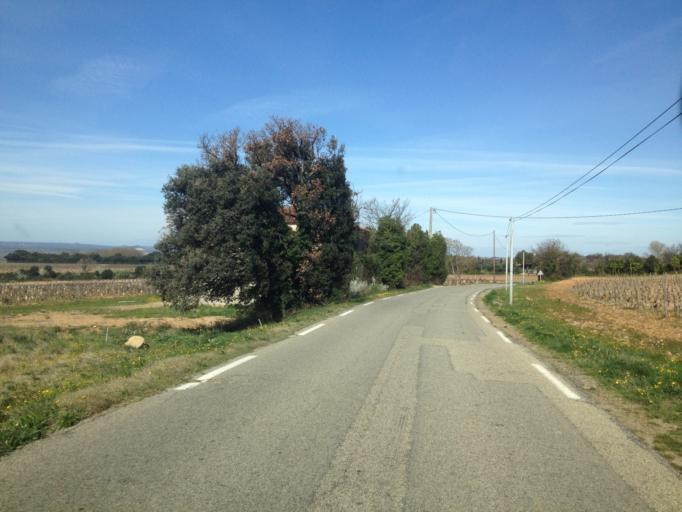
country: FR
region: Provence-Alpes-Cote d'Azur
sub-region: Departement du Vaucluse
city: Bedarrides
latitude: 44.0487
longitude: 4.8698
